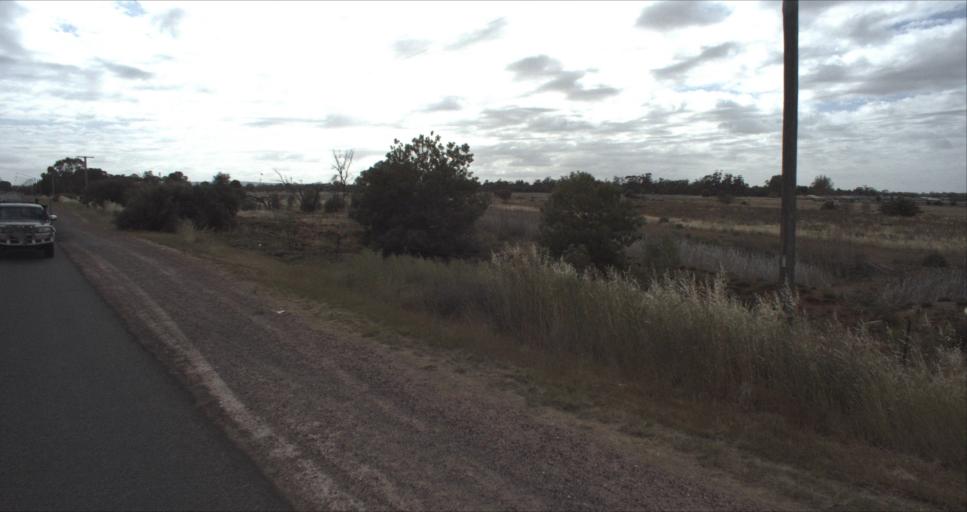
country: AU
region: New South Wales
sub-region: Leeton
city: Leeton
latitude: -34.5665
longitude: 146.3968
